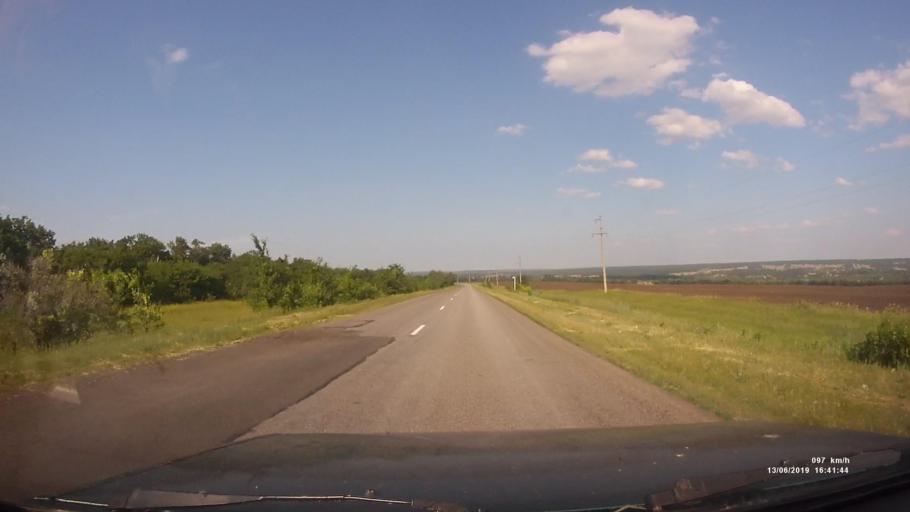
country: RU
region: Rostov
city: Kazanskaya
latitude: 49.9374
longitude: 41.3892
